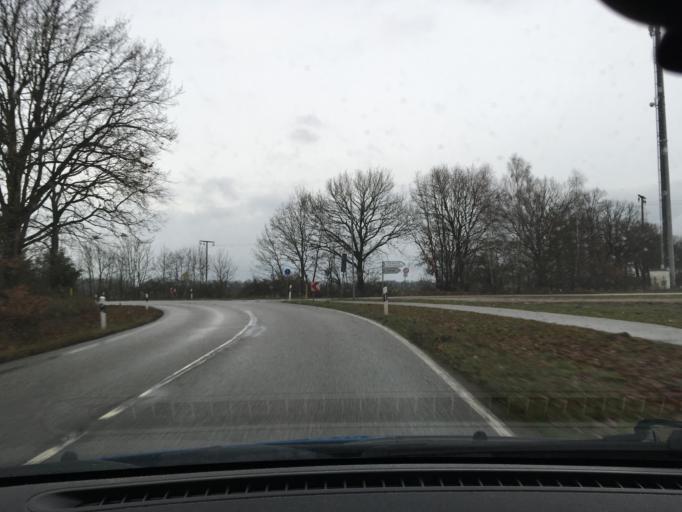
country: DE
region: Schleswig-Holstein
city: Lanze
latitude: 53.3772
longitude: 10.6305
